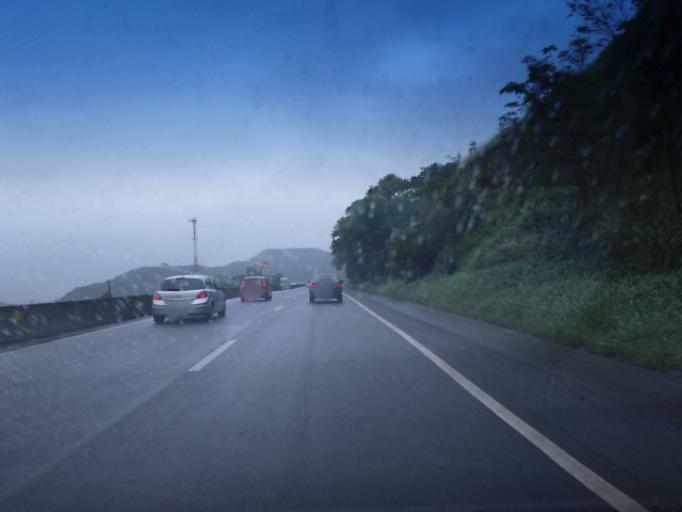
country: BR
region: Santa Catarina
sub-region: Penha
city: Penha
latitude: -26.8260
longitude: -48.6903
